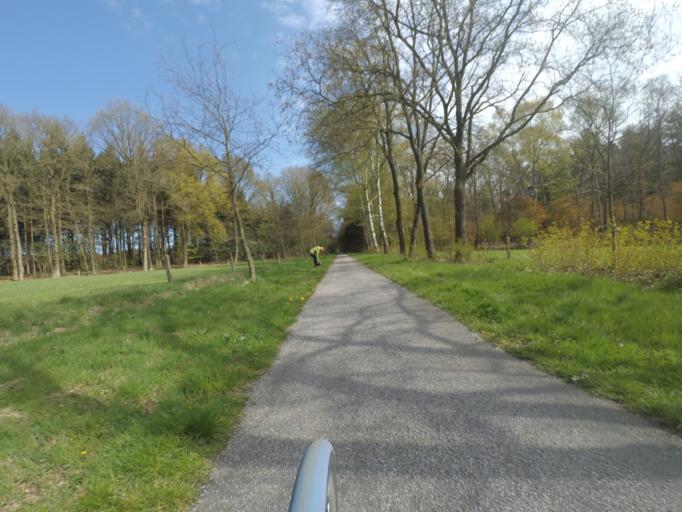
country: NL
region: Gelderland
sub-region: Gemeente Epe
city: Epe
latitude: 52.3652
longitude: 5.9968
